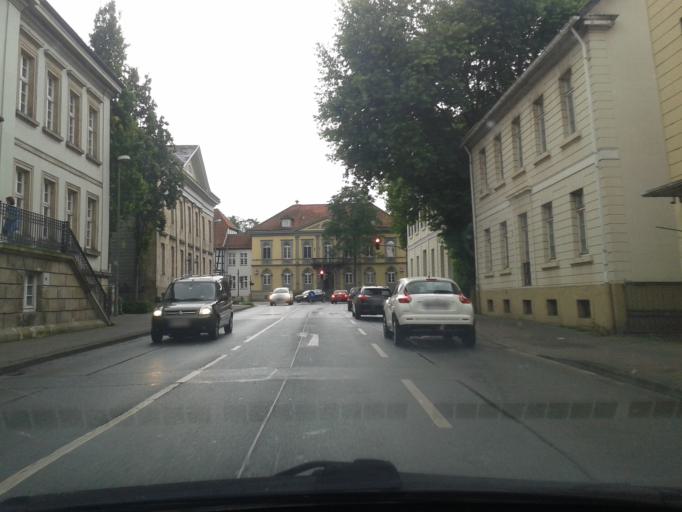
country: DE
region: North Rhine-Westphalia
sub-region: Regierungsbezirk Detmold
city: Detmold
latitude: 51.9325
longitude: 8.8809
